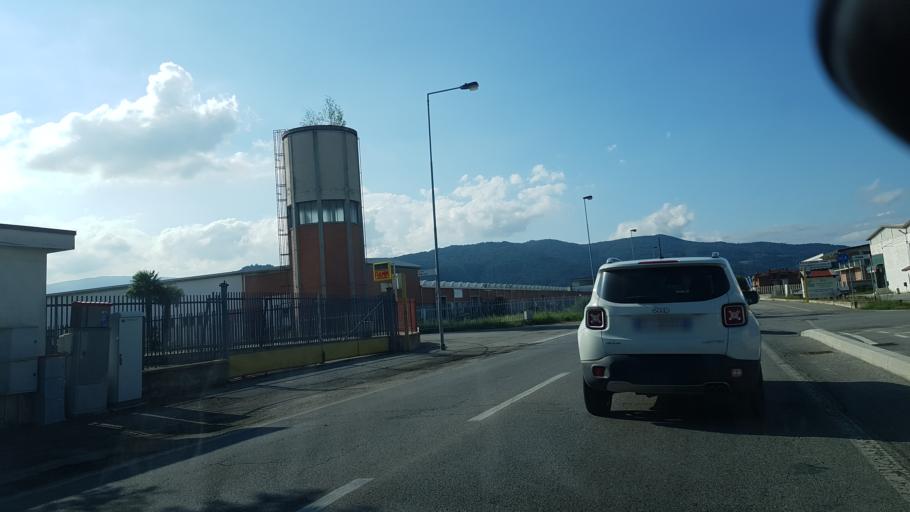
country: IT
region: Piedmont
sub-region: Provincia di Cuneo
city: Busca
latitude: 44.5028
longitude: 7.4900
